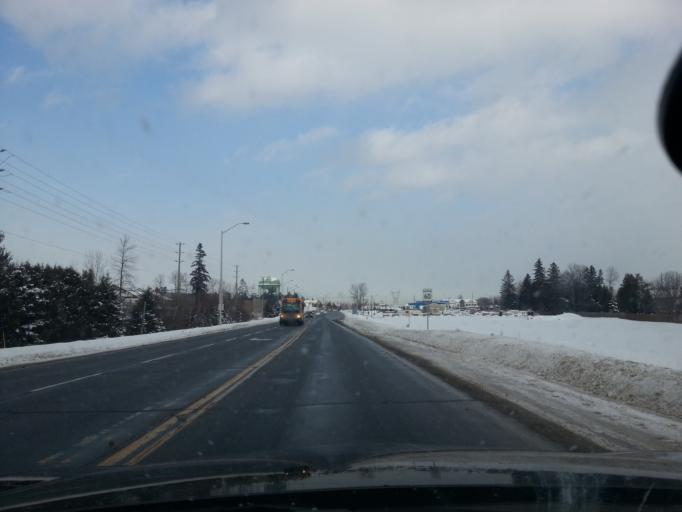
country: CA
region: Ontario
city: Bells Corners
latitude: 45.2639
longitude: -75.9428
